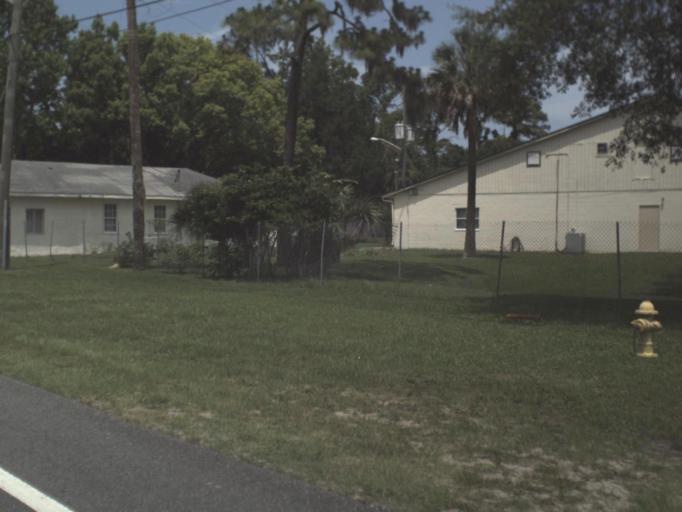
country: US
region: Florida
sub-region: Nassau County
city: Yulee
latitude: 30.4823
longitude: -81.6277
